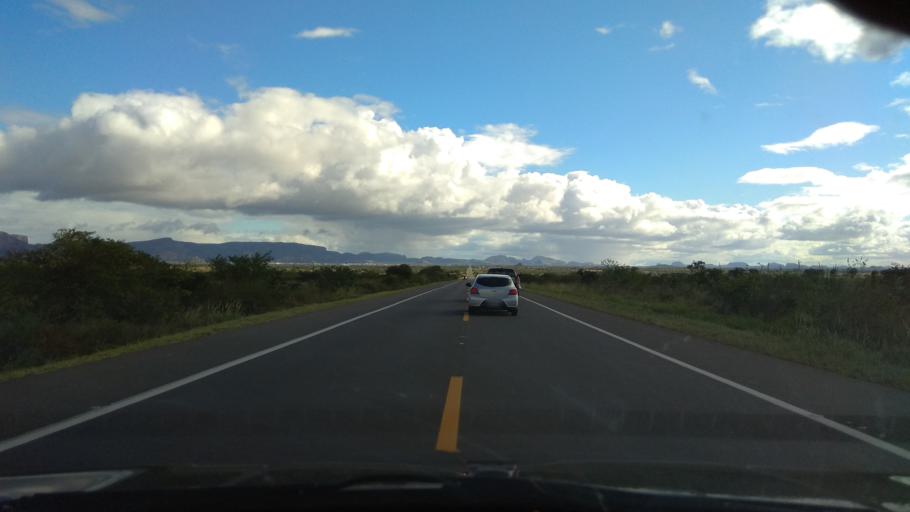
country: BR
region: Bahia
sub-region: Castro Alves
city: Castro Alves
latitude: -12.6633
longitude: -39.6350
